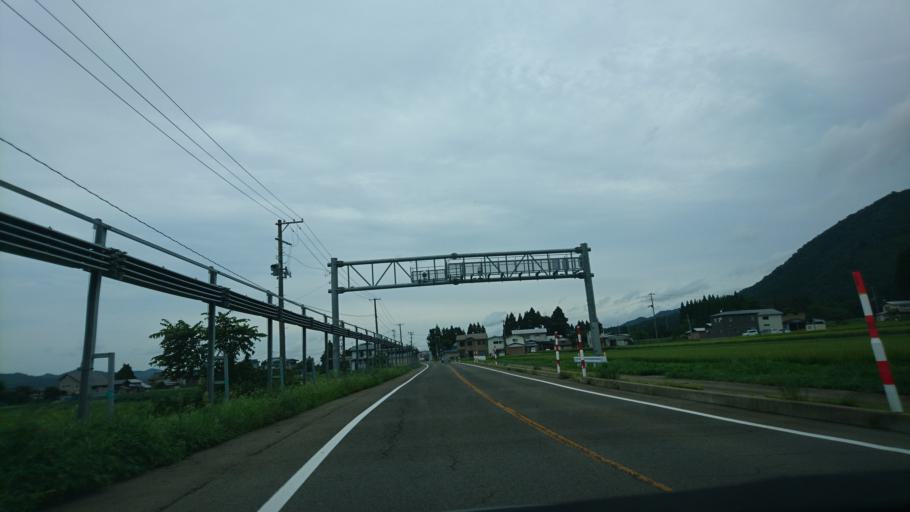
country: JP
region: Akita
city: Yuzawa
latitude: 39.1242
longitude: 140.5771
